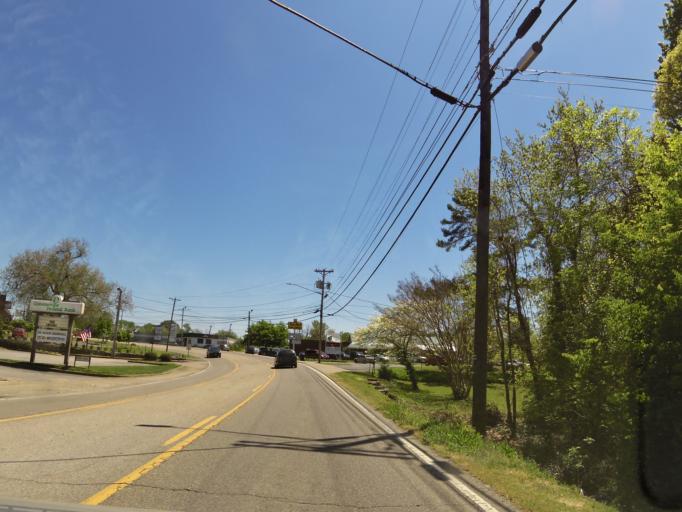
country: US
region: Tennessee
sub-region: Greene County
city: Greeneville
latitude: 36.1686
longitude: -82.8132
